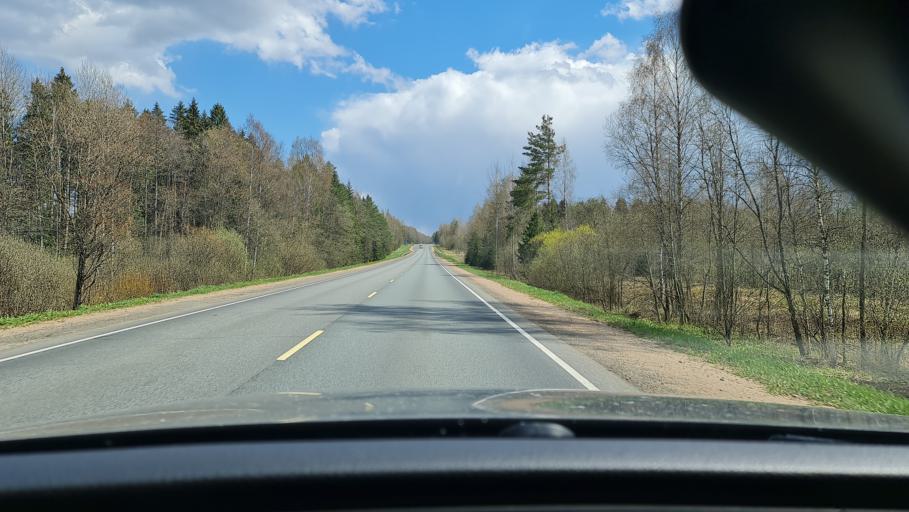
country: RU
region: Tverskaya
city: Zapadnaya Dvina
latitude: 56.3044
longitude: 32.2357
